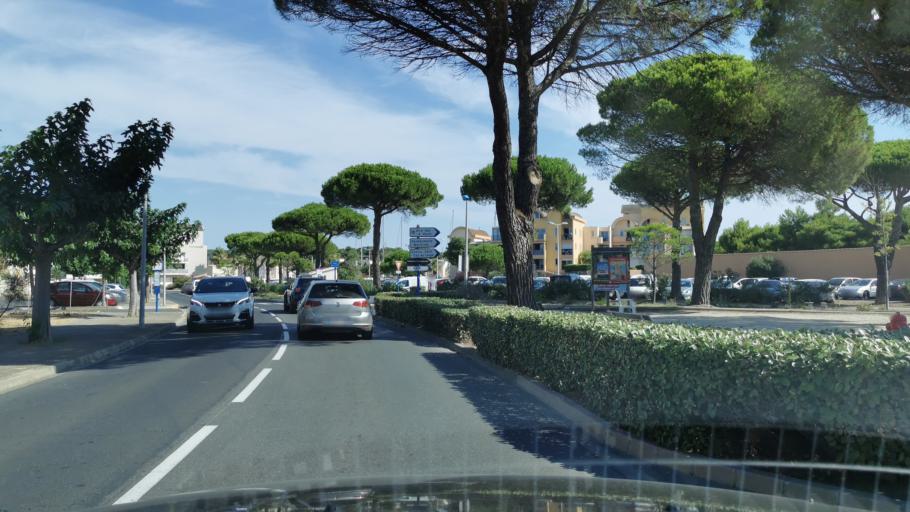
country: FR
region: Languedoc-Roussillon
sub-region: Departement de l'Aude
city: Gruissan
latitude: 43.1058
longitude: 3.0963
